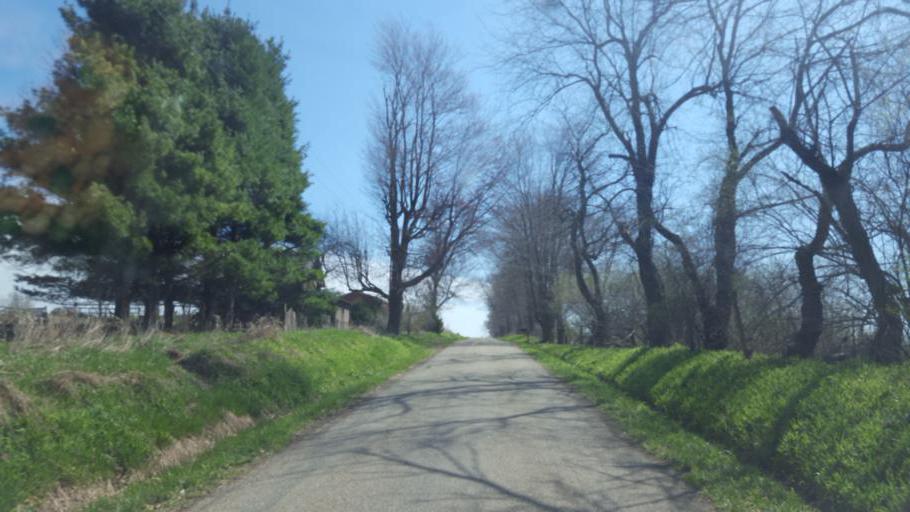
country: US
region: Ohio
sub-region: Knox County
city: Gambier
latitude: 40.3476
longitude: -82.3776
